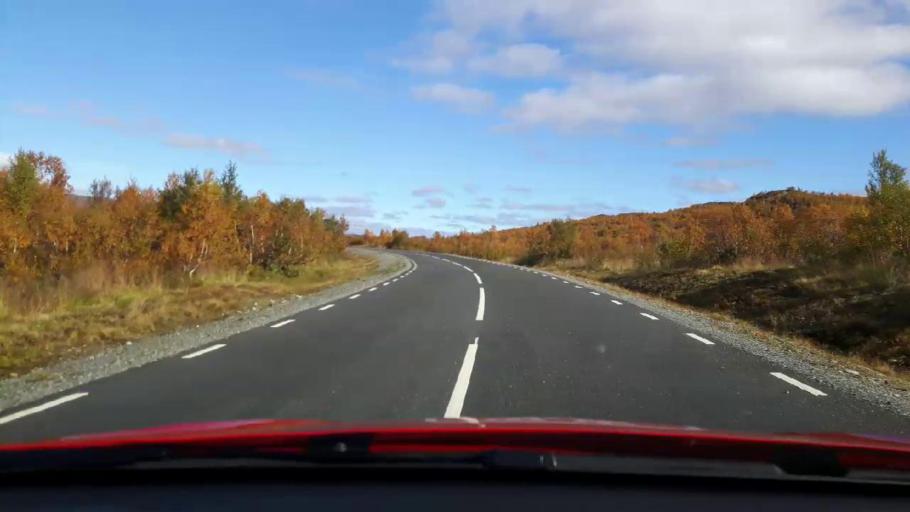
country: NO
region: Nordland
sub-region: Hattfjelldal
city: Hattfjelldal
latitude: 64.9961
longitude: 14.2371
